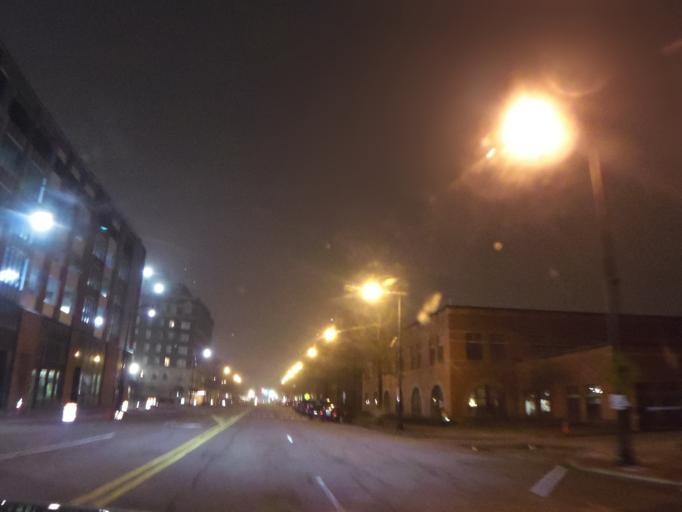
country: US
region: North Carolina
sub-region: Cumberland County
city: Fayetteville
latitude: 35.0548
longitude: -78.8848
